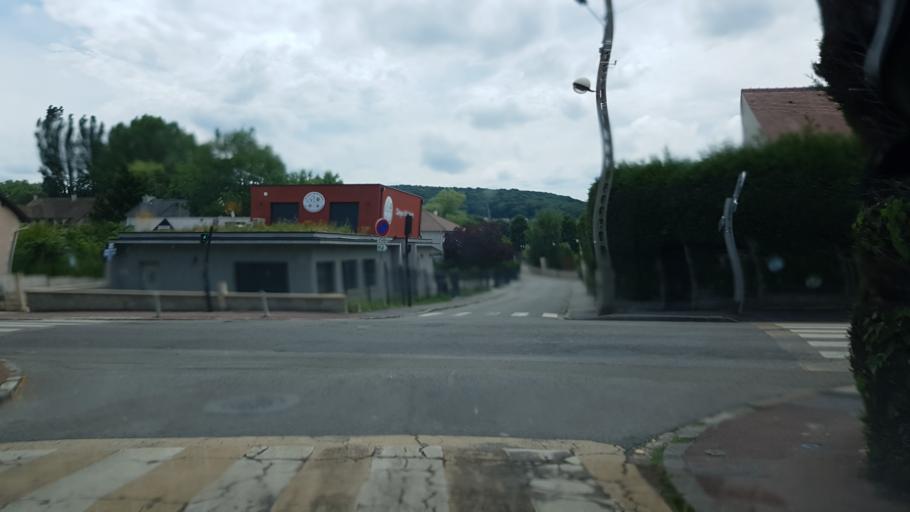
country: FR
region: Ile-de-France
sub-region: Departement des Yvelines
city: Saint-Remy-les-Chevreuse
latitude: 48.7076
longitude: 2.0690
